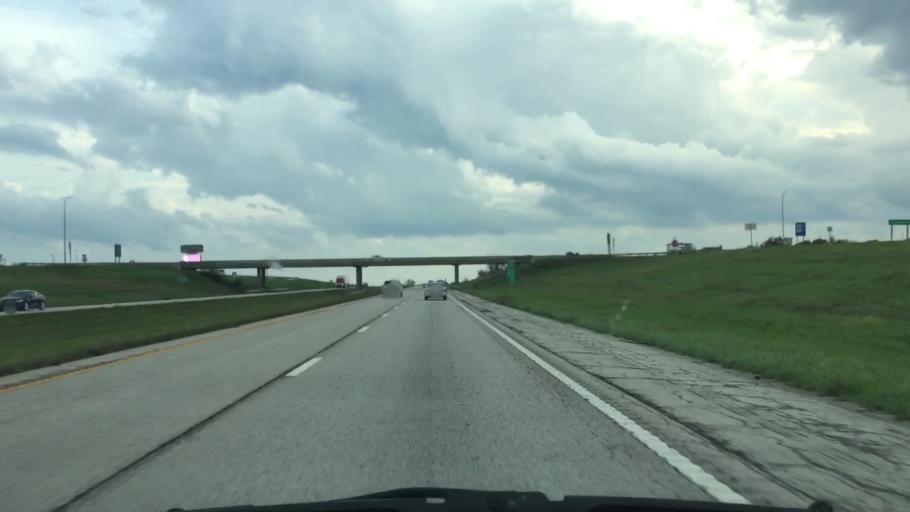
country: US
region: Missouri
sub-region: Clinton County
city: Cameron
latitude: 39.7332
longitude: -94.2207
